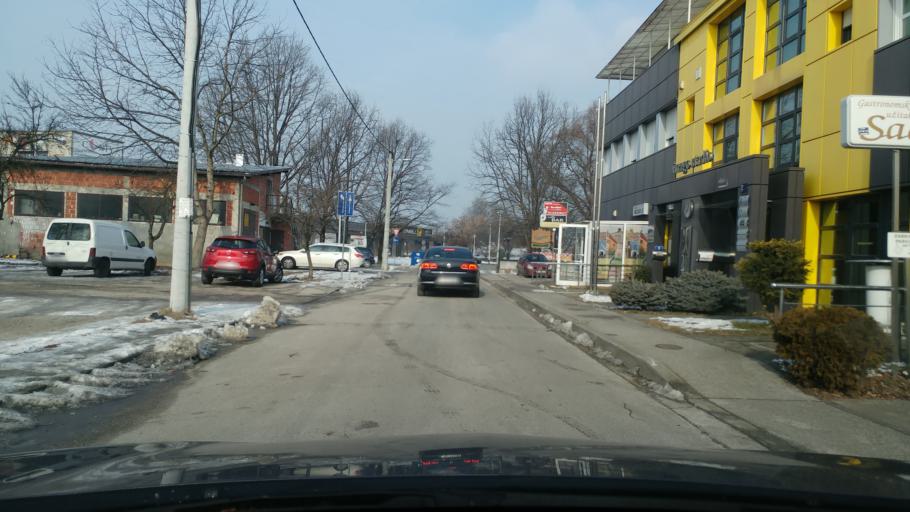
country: HR
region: Grad Zagreb
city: Novi Zagreb
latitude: 45.7758
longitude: 15.9598
